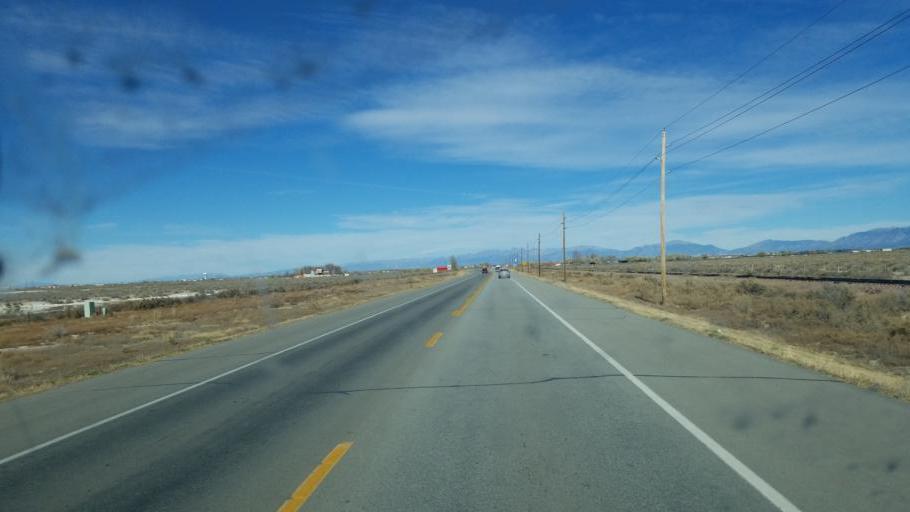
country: US
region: Colorado
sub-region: Alamosa County
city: Alamosa
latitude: 37.4231
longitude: -105.8944
